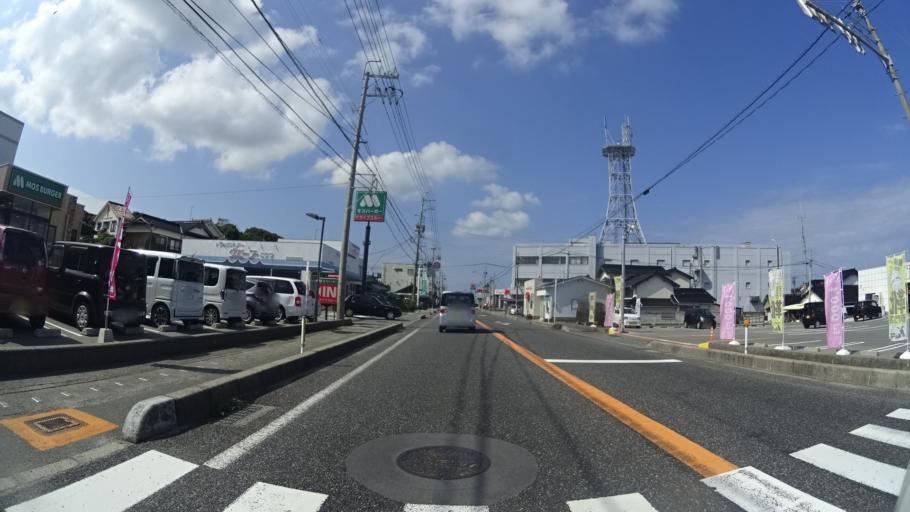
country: JP
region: Shimane
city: Gotsucho
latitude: 35.0101
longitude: 132.2183
